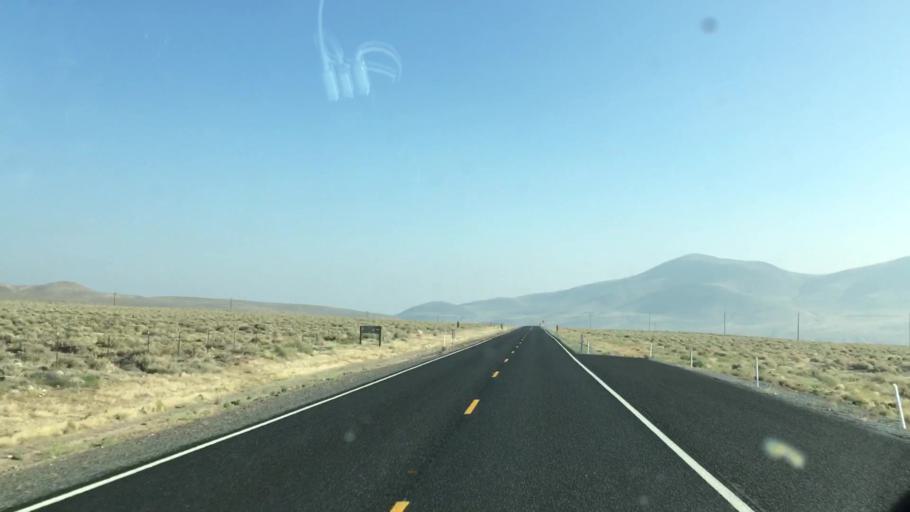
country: US
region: Nevada
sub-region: Lyon County
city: Fernley
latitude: 39.7278
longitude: -119.3335
